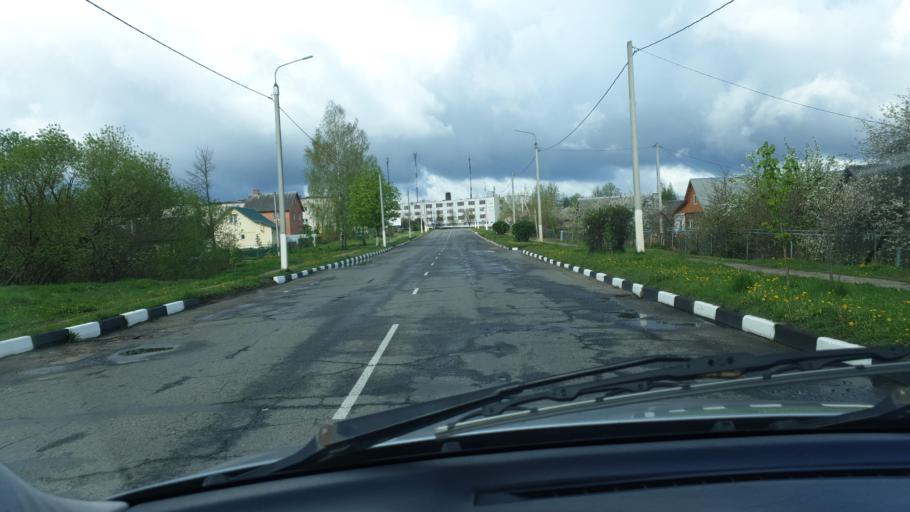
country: BY
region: Vitebsk
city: Lyepyel'
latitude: 54.8756
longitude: 28.6834
